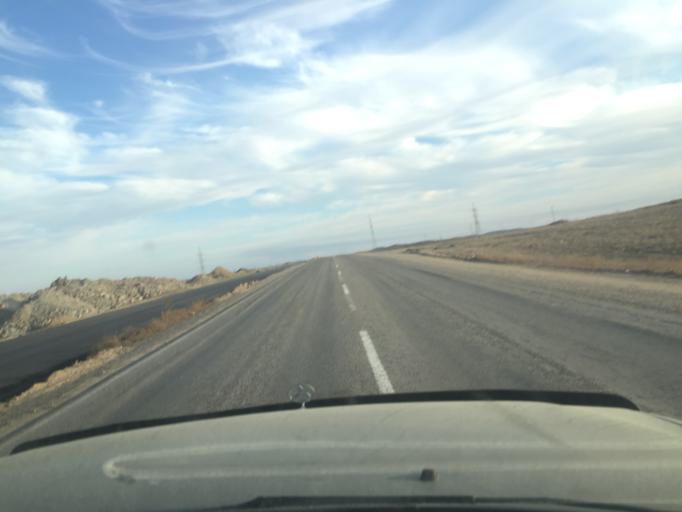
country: KZ
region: Almaty Oblysy
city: Ulken
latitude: 45.2156
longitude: 73.8686
